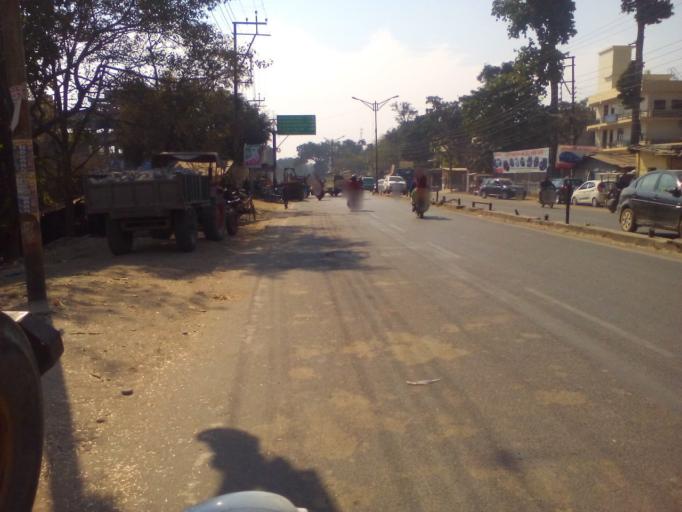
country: IN
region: Uttarakhand
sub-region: Dehradun
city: Dehradun
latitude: 30.3150
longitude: 78.0254
